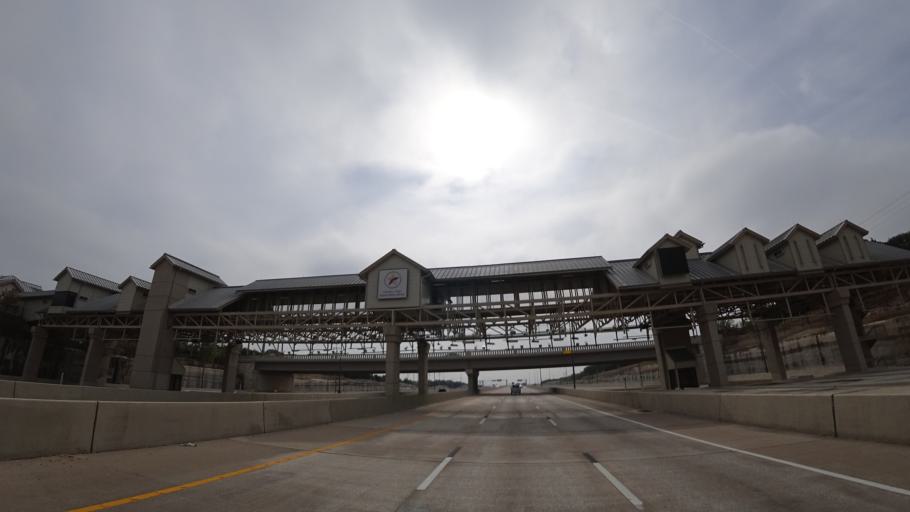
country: US
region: Texas
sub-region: Williamson County
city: Cedar Park
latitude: 30.5145
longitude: -97.8134
